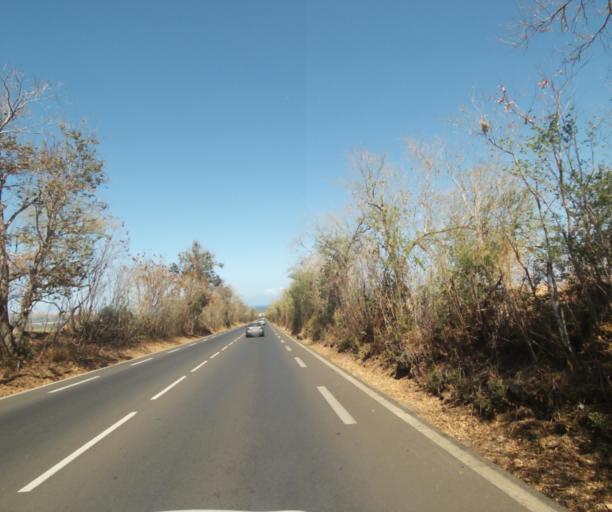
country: RE
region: Reunion
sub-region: Reunion
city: Le Port
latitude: -20.9816
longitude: 55.3104
